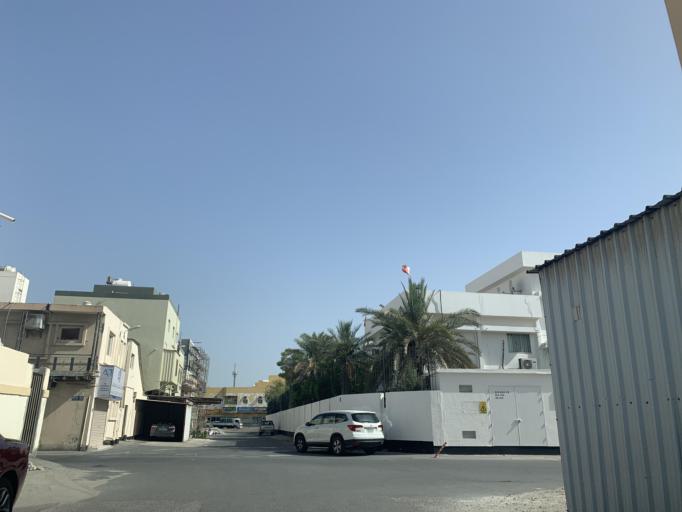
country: BH
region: Northern
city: Sitrah
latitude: 26.1642
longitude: 50.6120
